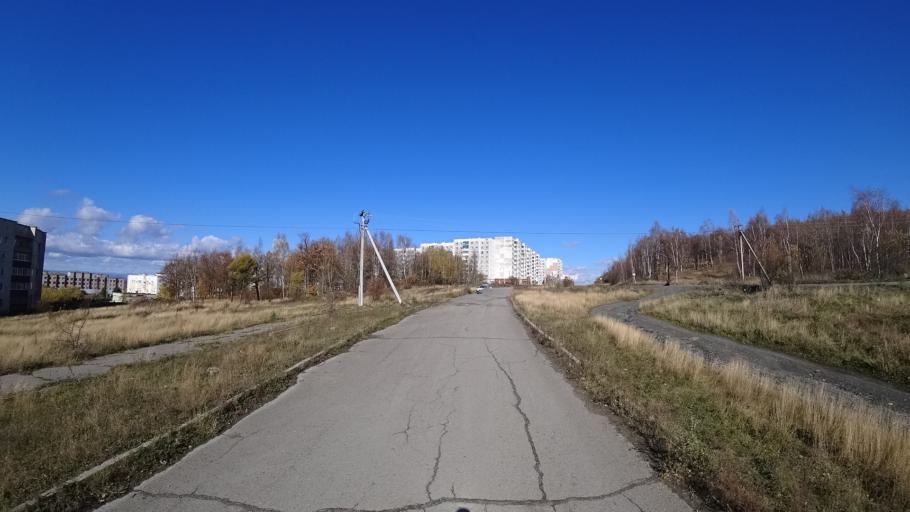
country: RU
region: Khabarovsk Krai
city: Amursk
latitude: 50.2410
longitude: 136.9197
